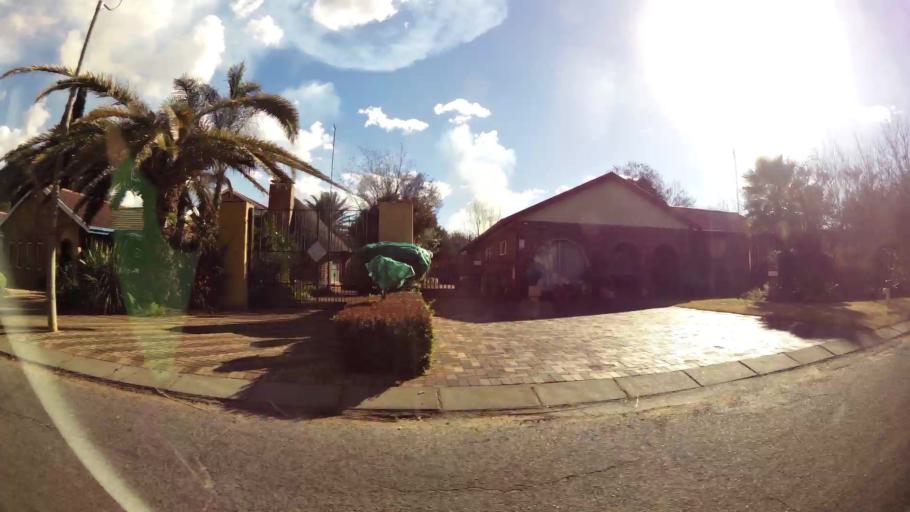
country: ZA
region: North-West
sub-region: Dr Kenneth Kaunda District Municipality
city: Klerksdorp
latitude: -26.8306
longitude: 26.6804
